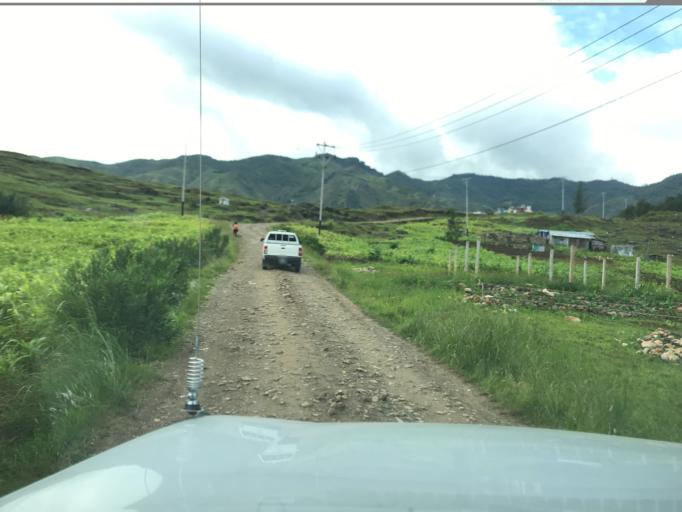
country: TL
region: Aileu
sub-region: Aileu Villa
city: Aileu
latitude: -8.8547
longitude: 125.5790
